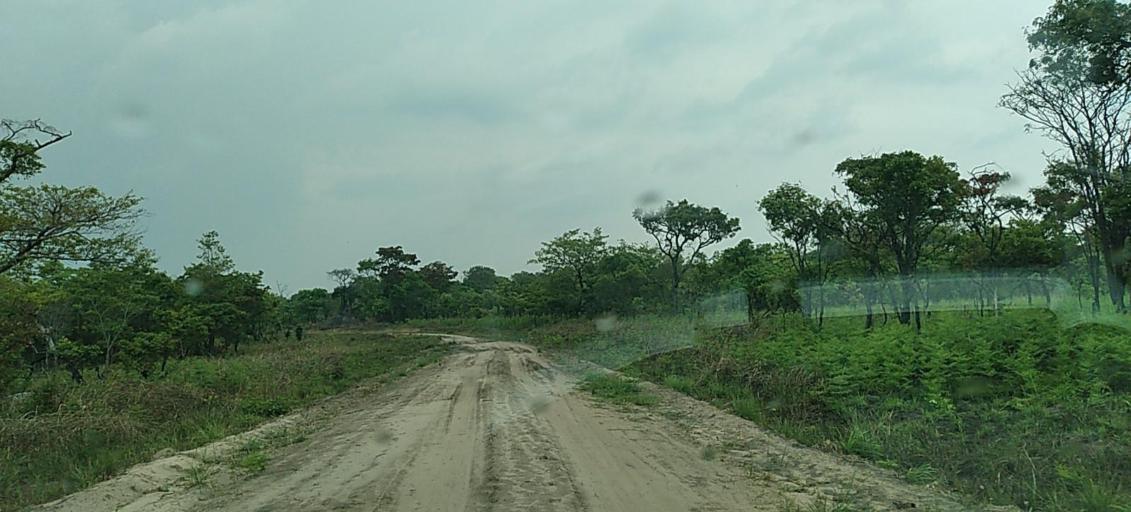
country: ZM
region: North-Western
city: Mwinilunga
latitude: -11.4276
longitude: 24.5914
